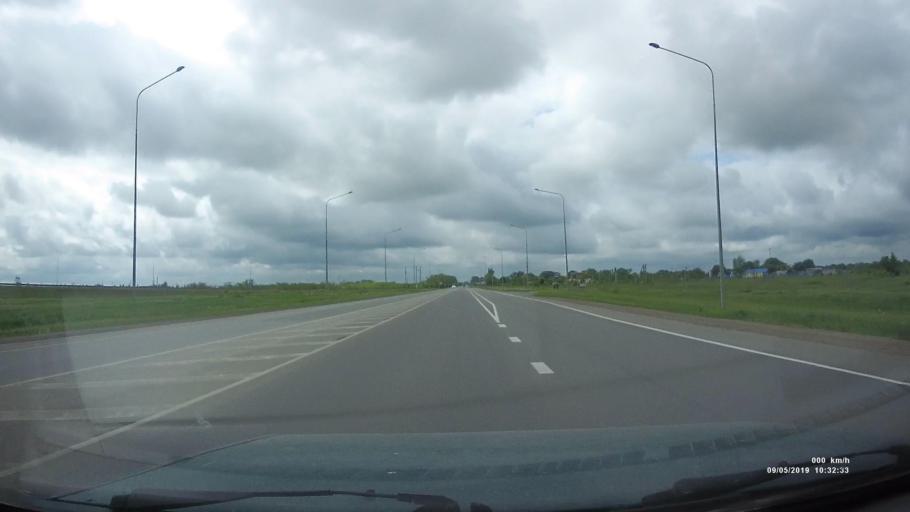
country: RU
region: Rostov
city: Azov
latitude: 47.0709
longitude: 39.4260
